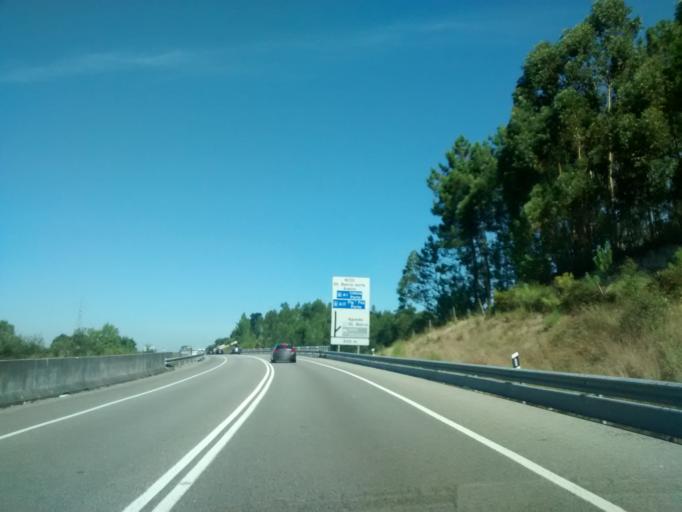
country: PT
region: Aveiro
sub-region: Oliveira do Bairro
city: Oliveira do Bairro
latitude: 40.5090
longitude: -8.4941
